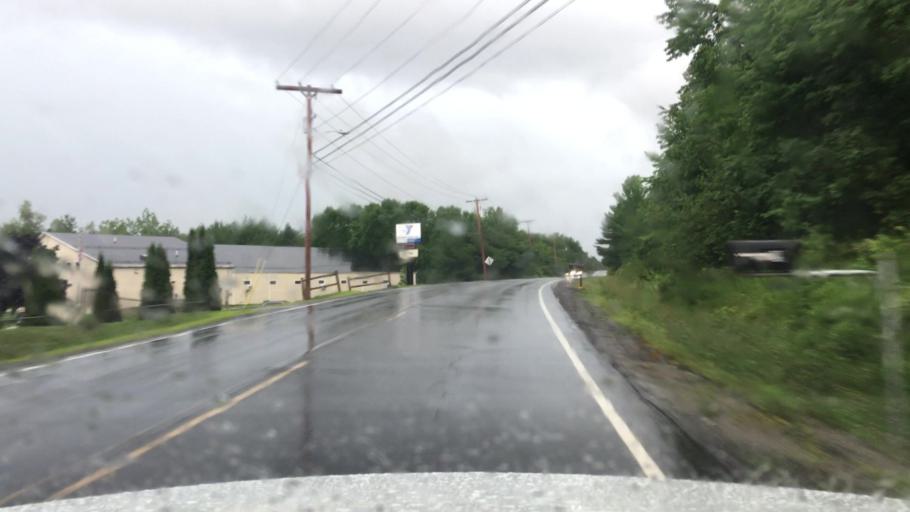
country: US
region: Maine
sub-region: Kennebec County
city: Manchester
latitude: 44.3243
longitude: -69.8559
